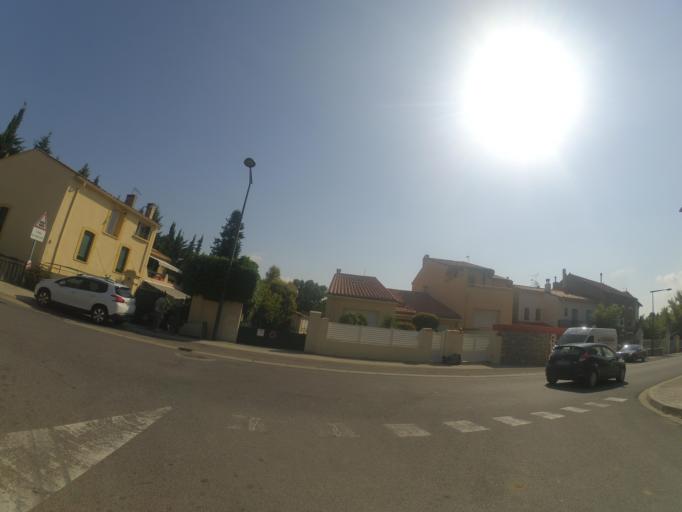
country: FR
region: Languedoc-Roussillon
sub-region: Departement des Pyrenees-Orientales
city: Ille-sur-Tet
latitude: 42.6684
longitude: 2.6260
